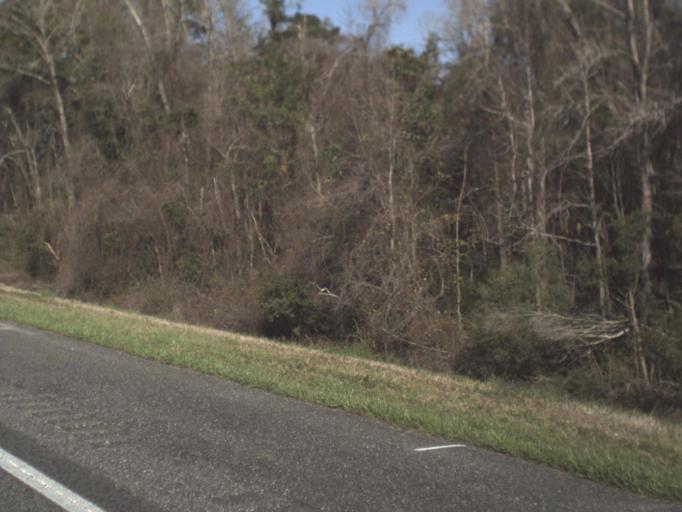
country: US
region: Florida
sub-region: Jefferson County
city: Monticello
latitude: 30.4733
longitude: -83.8619
